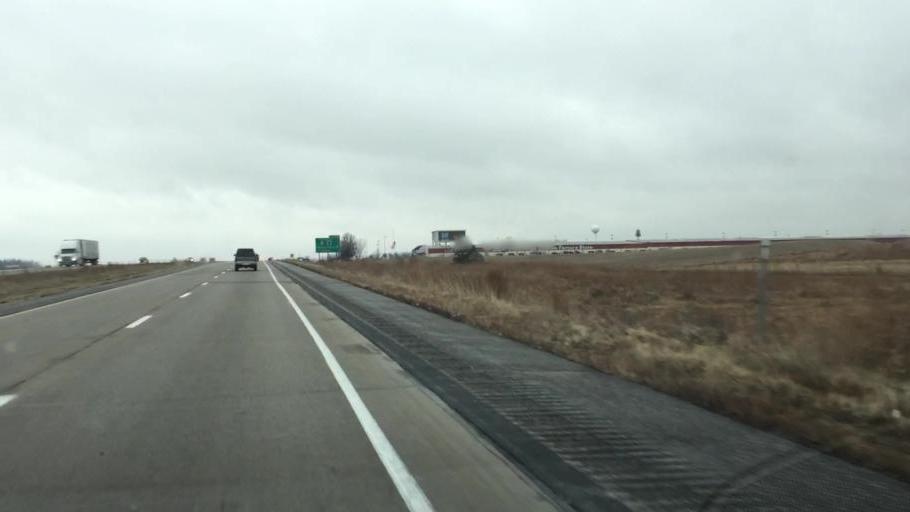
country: US
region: Iowa
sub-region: Iowa County
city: Williamsburg
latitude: 41.6872
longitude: -91.9980
